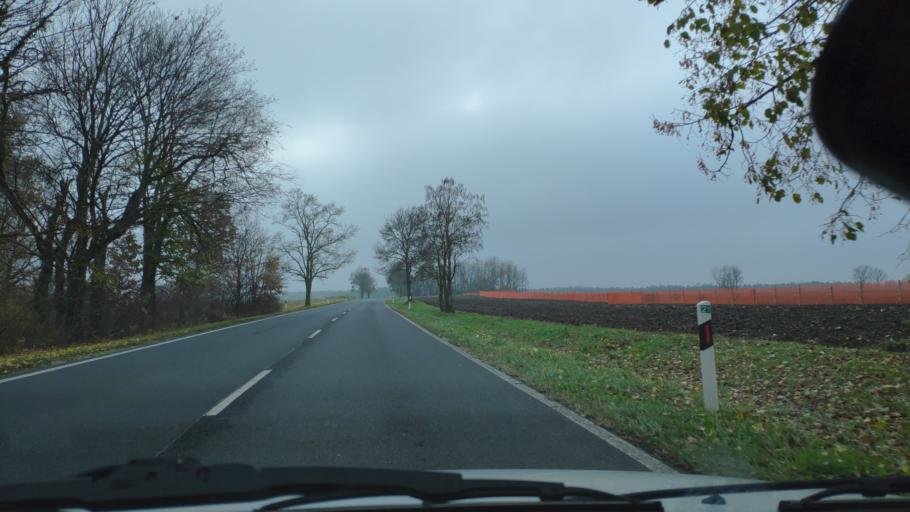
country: HU
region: Somogy
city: Balatonbereny
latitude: 46.6225
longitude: 17.2853
